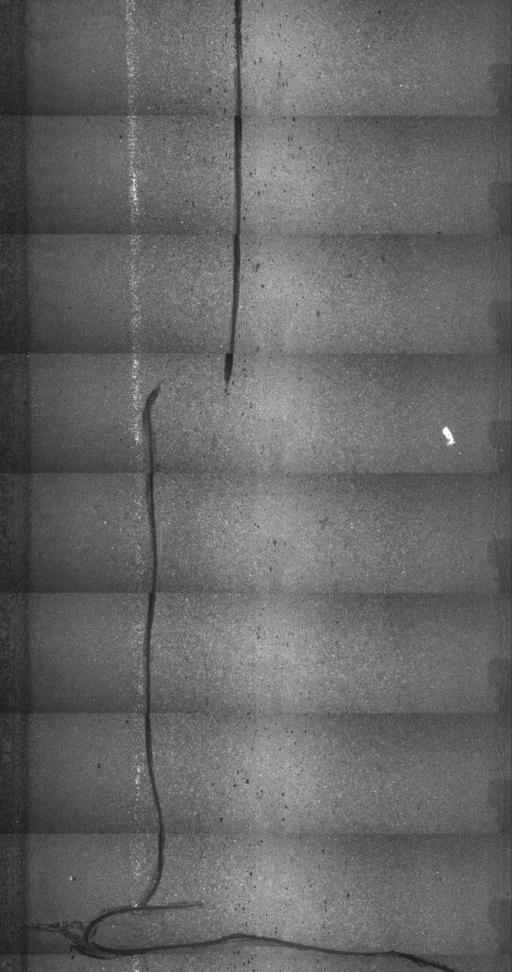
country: US
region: Vermont
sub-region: Orleans County
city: Newport
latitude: 44.9477
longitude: -72.3018
